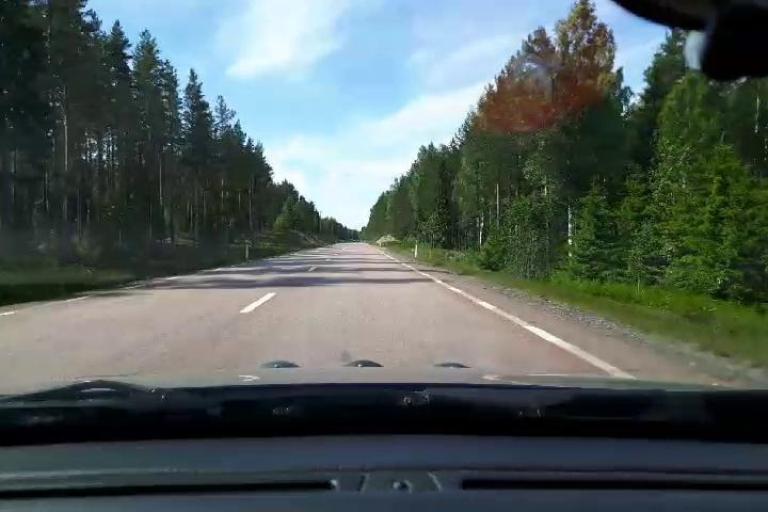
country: SE
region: Gaevleborg
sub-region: Soderhamns Kommun
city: Soderhamn
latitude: 61.1417
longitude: 16.9040
